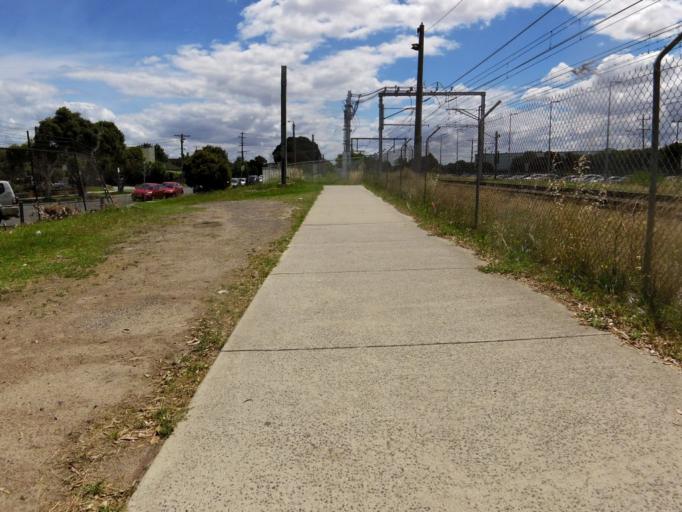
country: AU
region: Victoria
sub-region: Greater Dandenong
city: Springvale
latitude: -37.9369
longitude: 145.1366
